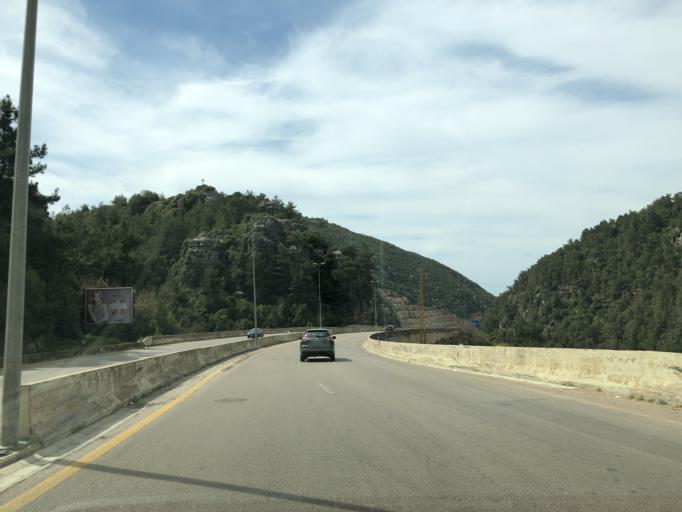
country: LB
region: Mont-Liban
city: Bhamdoun el Mhatta
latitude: 33.8947
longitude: 35.6565
